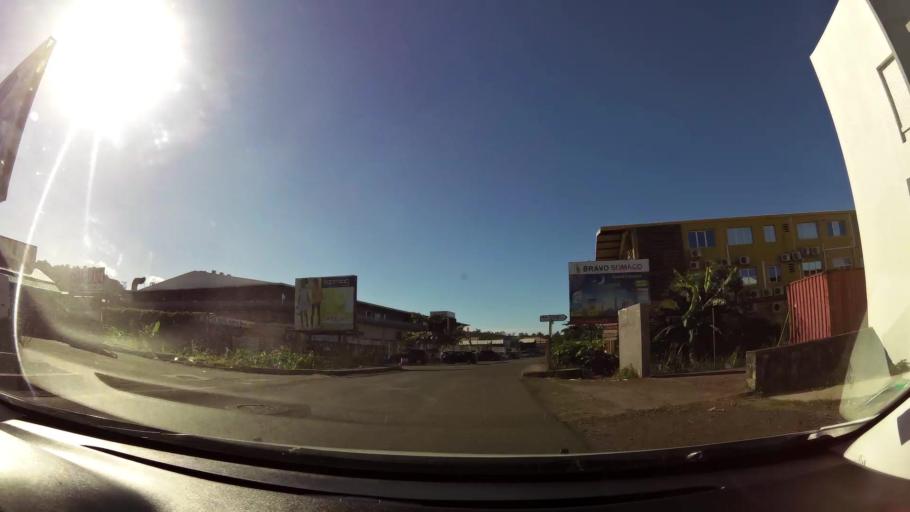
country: YT
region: Mamoudzou
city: Mamoudzou
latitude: -12.7728
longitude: 45.2249
